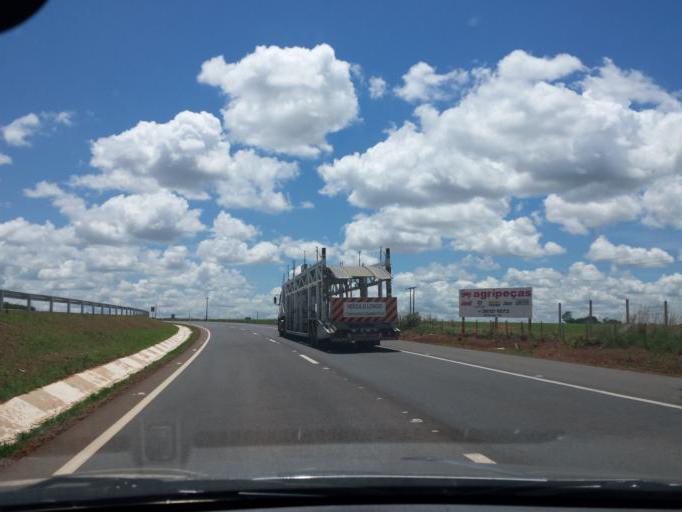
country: BR
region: Goias
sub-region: Cristalina
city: Cristalina
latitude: -16.7059
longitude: -47.6879
